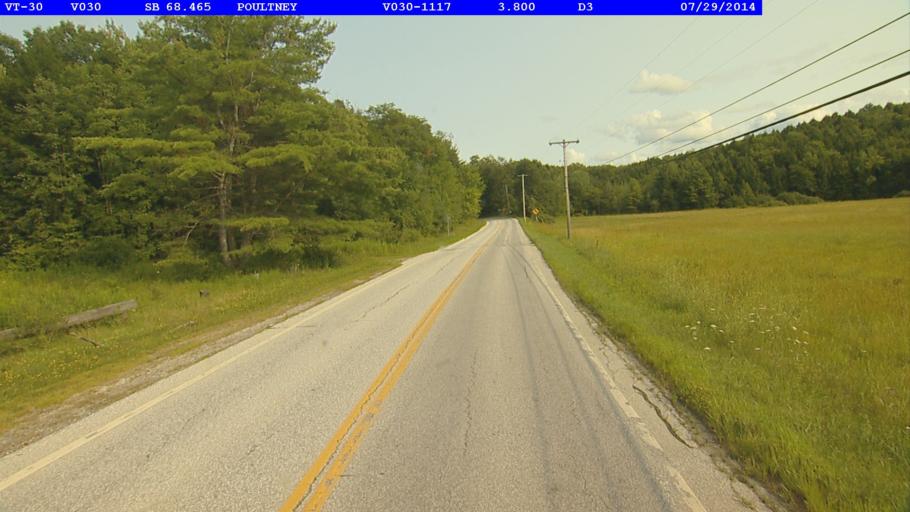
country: US
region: Vermont
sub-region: Rutland County
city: Poultney
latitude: 43.5124
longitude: -73.2215
